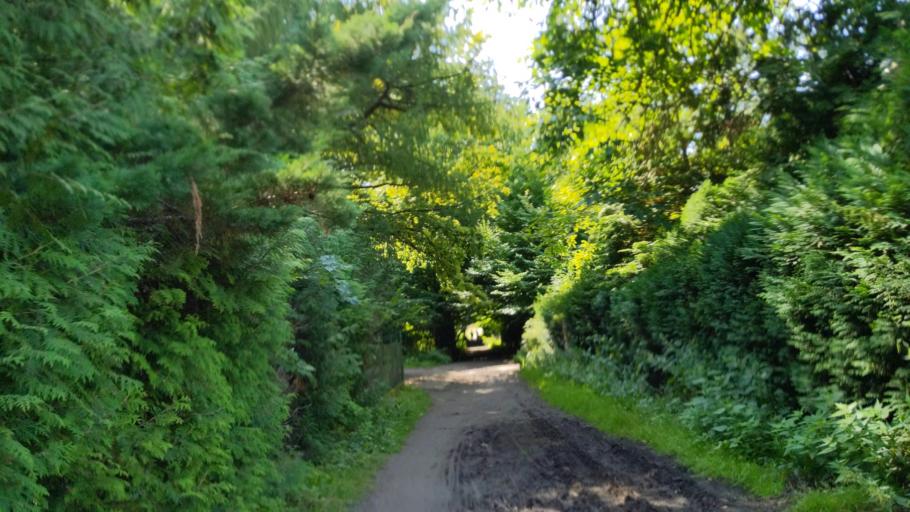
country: DE
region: Schleswig-Holstein
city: Bosdorf
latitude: 54.1599
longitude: 10.5055
